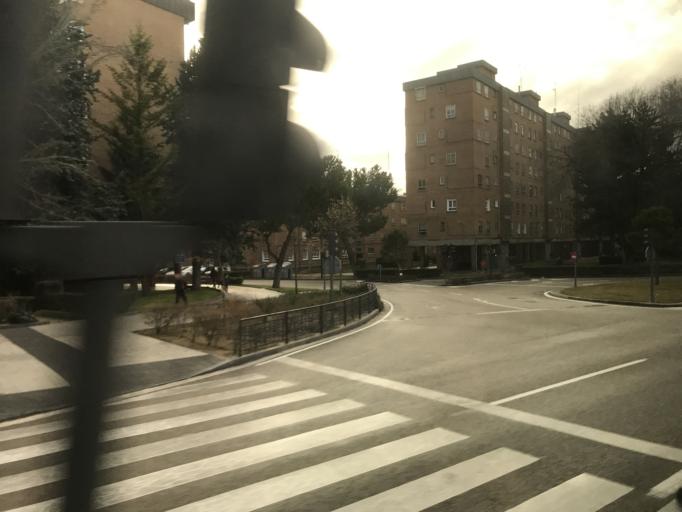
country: ES
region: Castille and Leon
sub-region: Provincia de Valladolid
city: Valladolid
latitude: 41.6467
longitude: -4.7391
